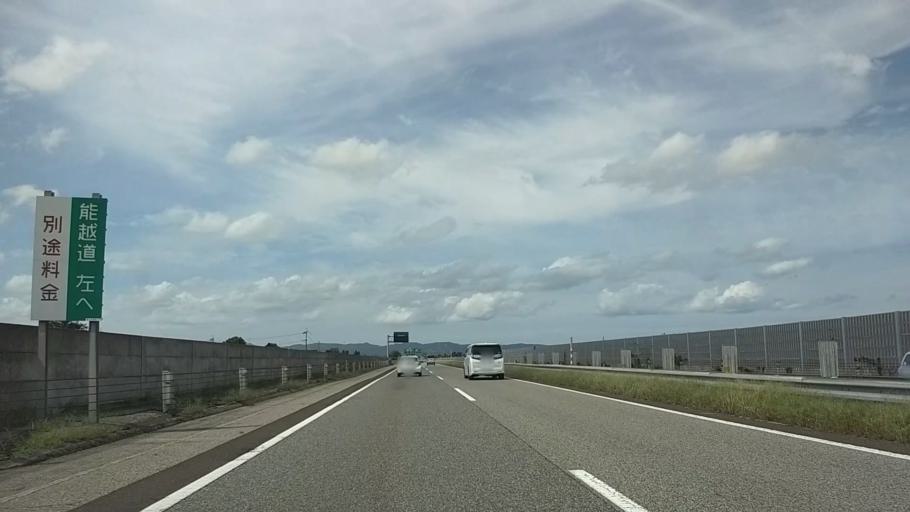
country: JP
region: Toyama
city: Nanto-shi
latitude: 36.6255
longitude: 136.9277
